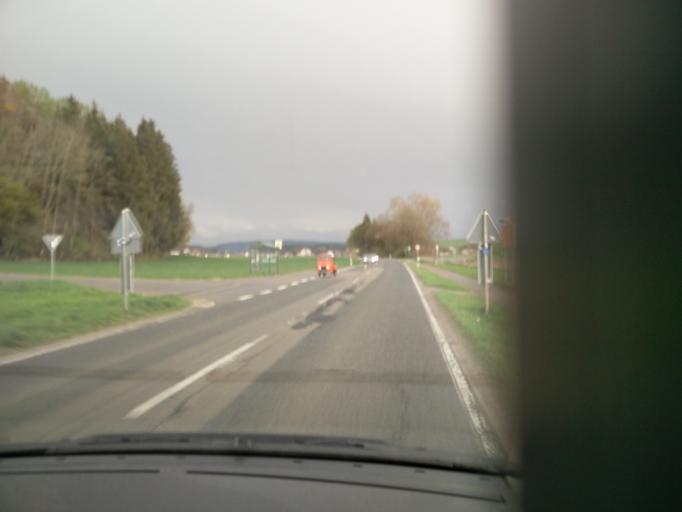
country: DE
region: Bavaria
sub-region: Upper Bavaria
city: Halfing
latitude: 47.9385
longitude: 12.2808
